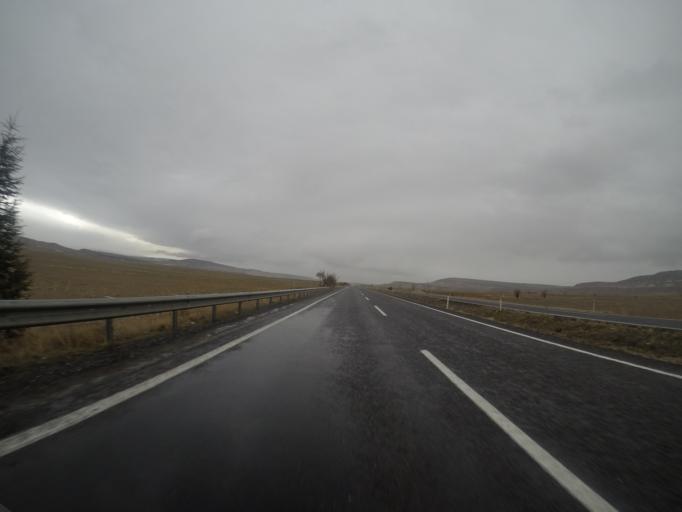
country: TR
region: Nevsehir
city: Urgub
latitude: 38.7232
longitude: 34.9513
